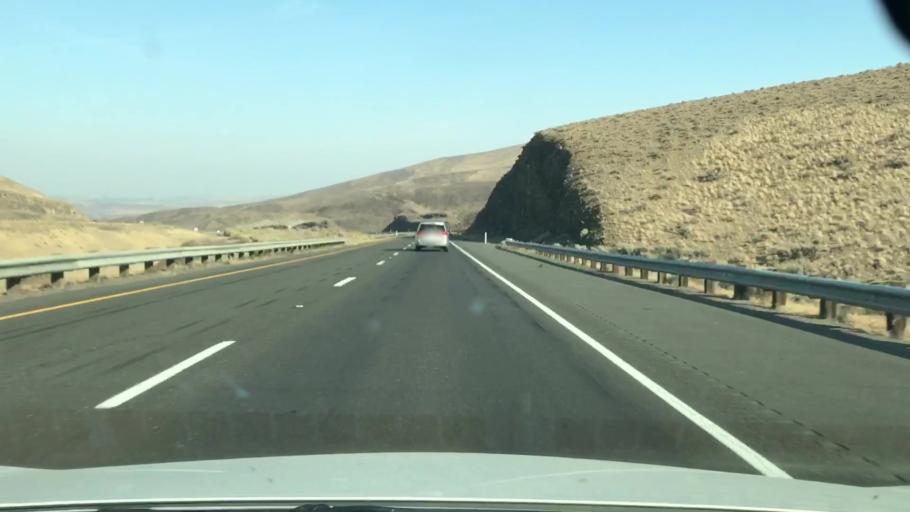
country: US
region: Washington
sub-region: Grant County
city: Mattawa
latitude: 46.9377
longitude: -120.0496
